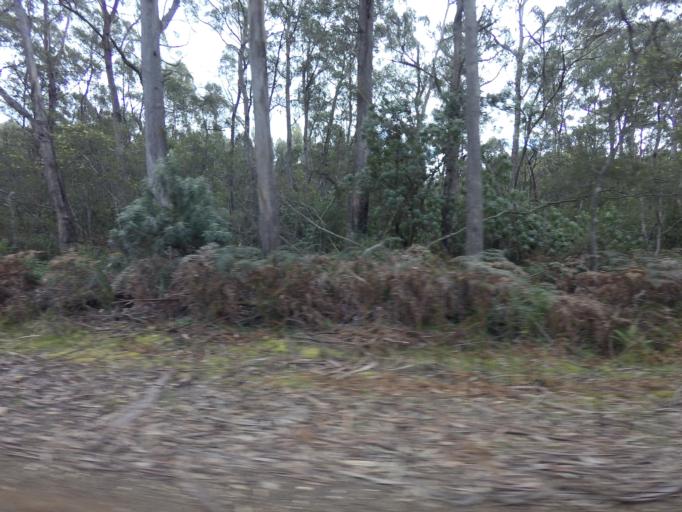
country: AU
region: Tasmania
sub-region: Huon Valley
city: Geeveston
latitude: -43.4242
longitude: 147.0073
